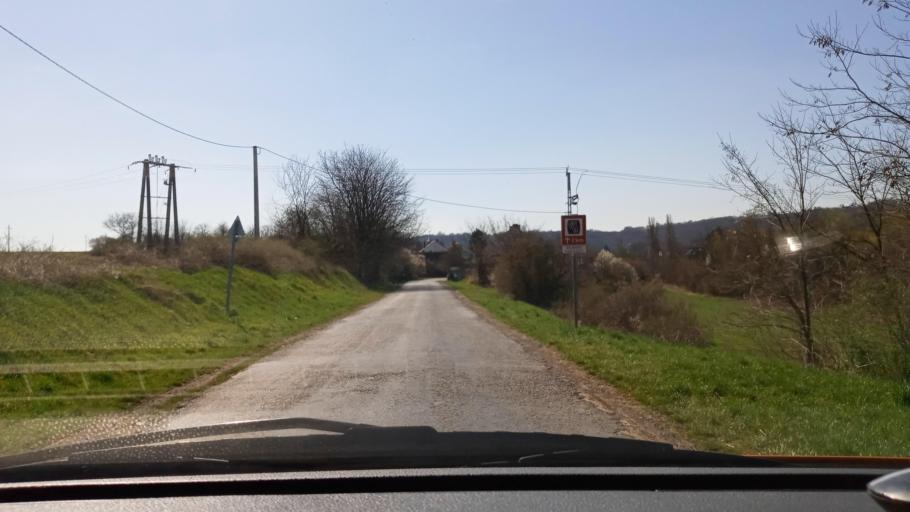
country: HU
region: Baranya
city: Kozarmisleny
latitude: 46.0381
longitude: 18.3870
